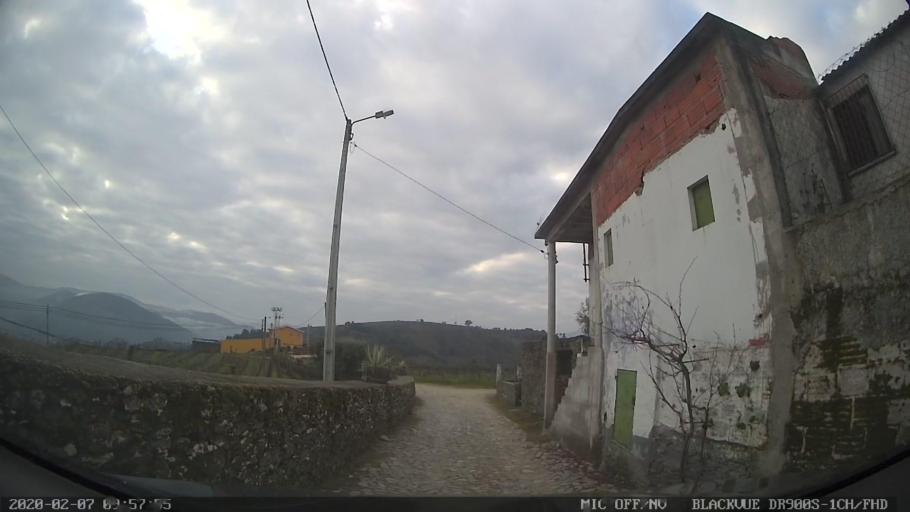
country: PT
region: Vila Real
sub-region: Sabrosa
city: Sabrosa
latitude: 41.2093
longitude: -7.5292
